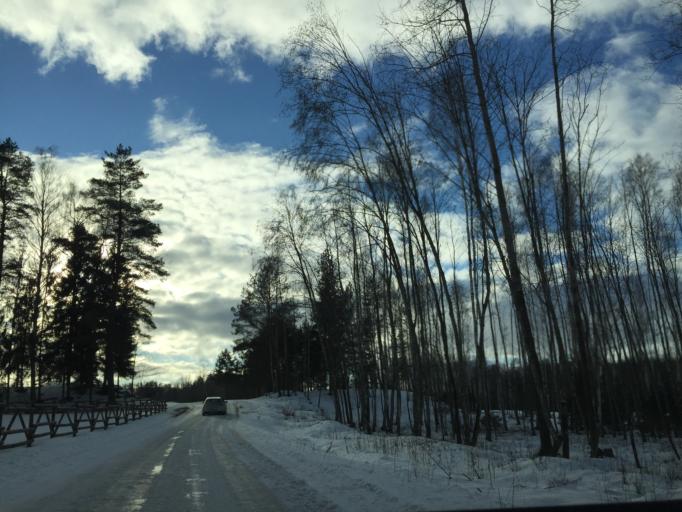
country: LV
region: Lielvarde
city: Lielvarde
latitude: 56.5691
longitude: 24.7972
